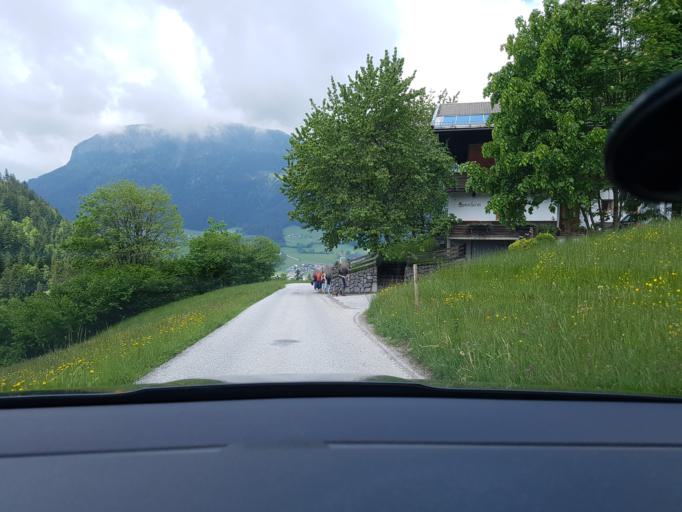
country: AT
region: Tyrol
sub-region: Politischer Bezirk Kufstein
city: Soll
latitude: 47.4924
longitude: 12.2025
